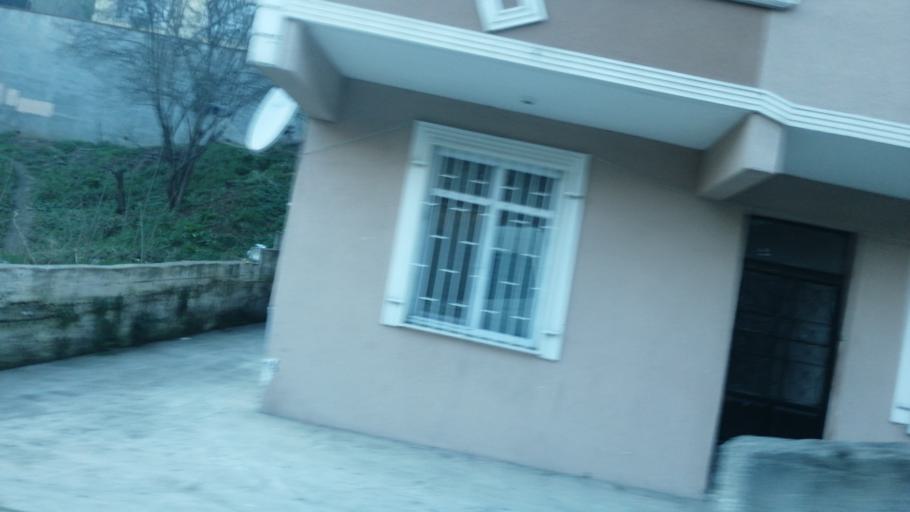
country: TR
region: Istanbul
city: UEskuedar
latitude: 41.0531
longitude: 29.0676
